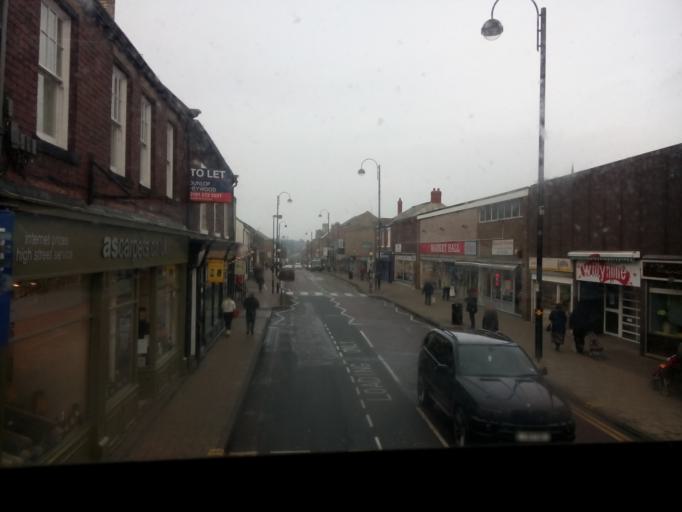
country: GB
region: England
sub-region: County Durham
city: Chester-le-Street
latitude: 54.8536
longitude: -1.5735
